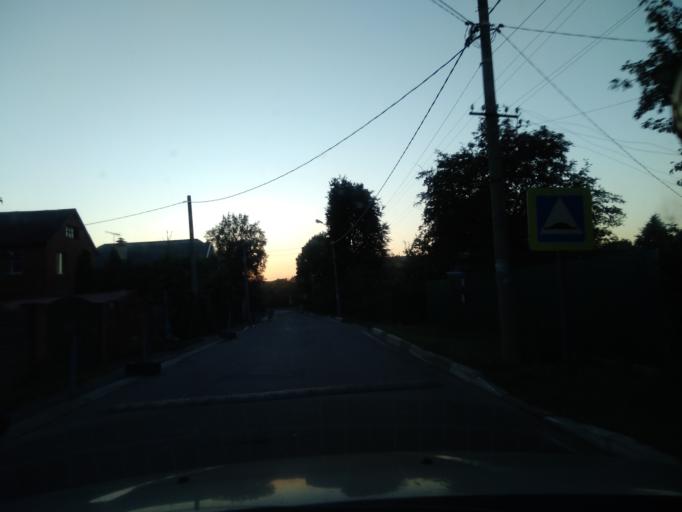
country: RU
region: Moscow
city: Strogino
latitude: 55.8621
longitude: 37.3886
